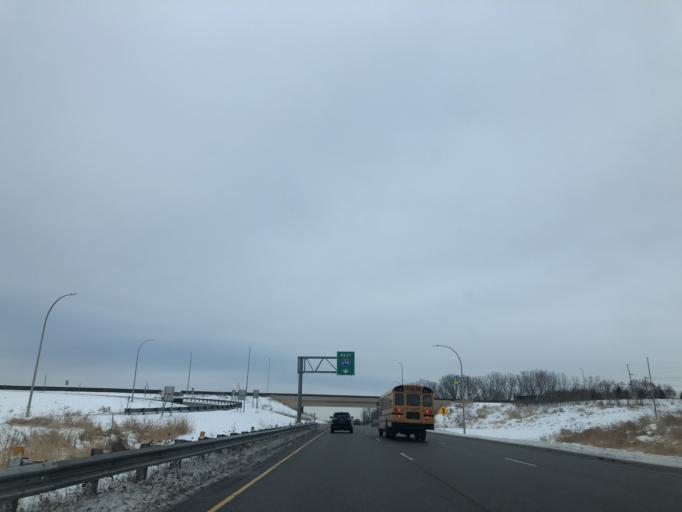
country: US
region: Minnesota
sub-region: Ramsey County
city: Arden Hills
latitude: 45.0624
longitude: -93.1561
